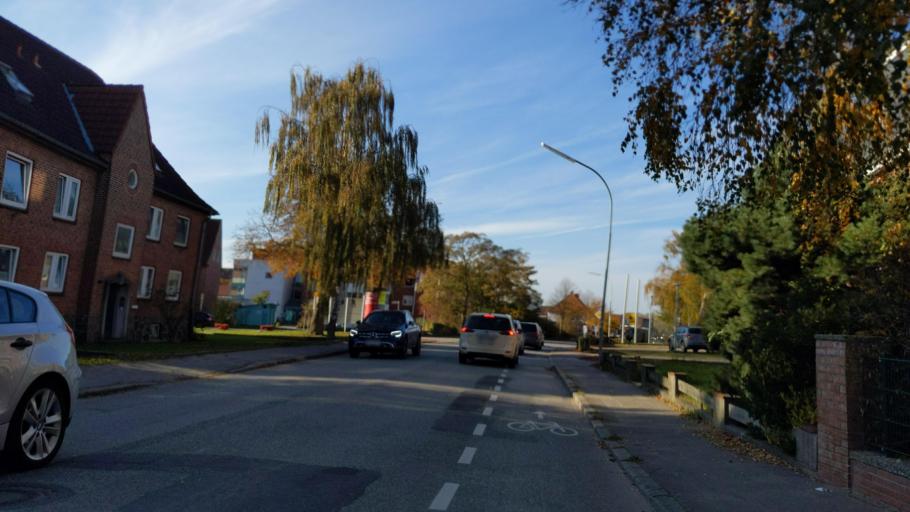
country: DE
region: Schleswig-Holstein
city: Eutin
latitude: 54.1296
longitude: 10.6200
